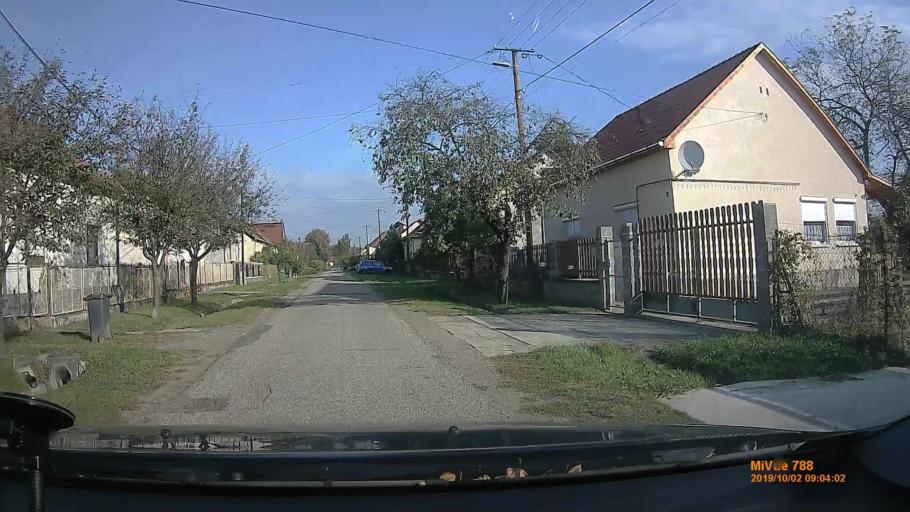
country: HU
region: Nograd
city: Batonyterenye
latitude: 48.0098
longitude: 19.8262
